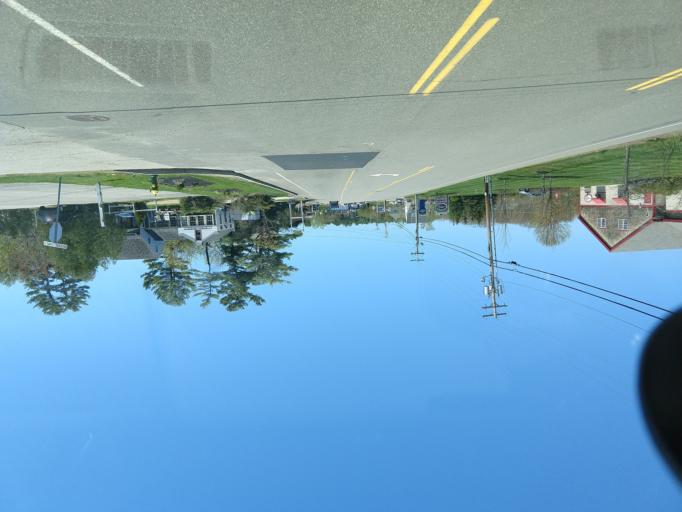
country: US
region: Maine
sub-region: York County
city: York Harbor
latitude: 43.1477
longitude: -70.6751
